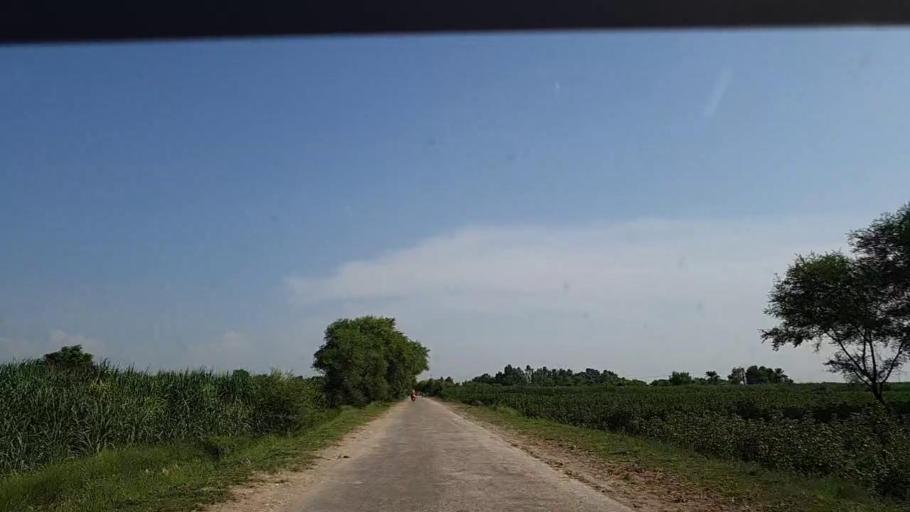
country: PK
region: Sindh
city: Adilpur
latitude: 27.9346
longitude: 69.2544
